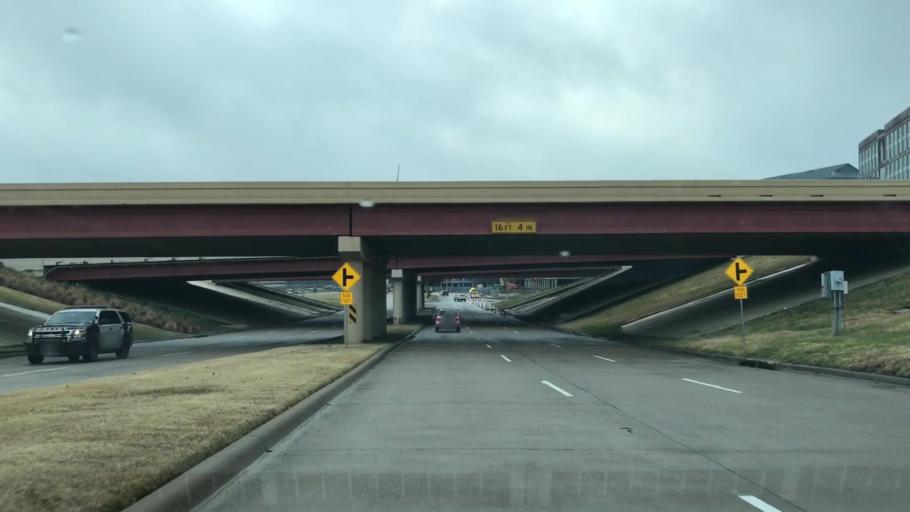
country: US
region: Texas
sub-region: Dallas County
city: Coppell
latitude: 32.8987
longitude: -96.9692
